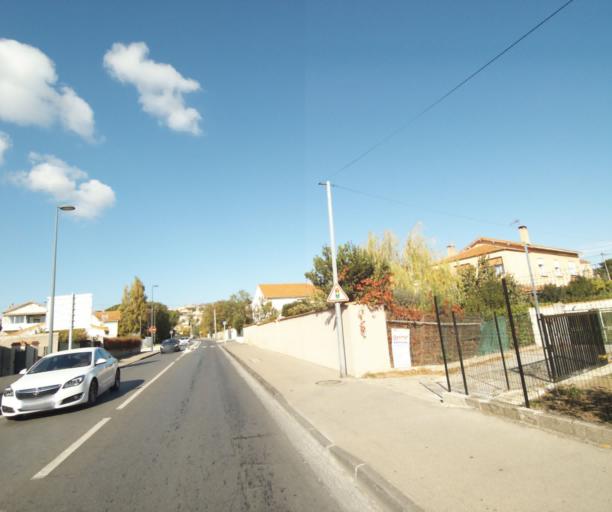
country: FR
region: Provence-Alpes-Cote d'Azur
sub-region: Departement des Bouches-du-Rhone
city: Plan-de-Cuques
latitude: 43.3445
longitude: 5.4585
